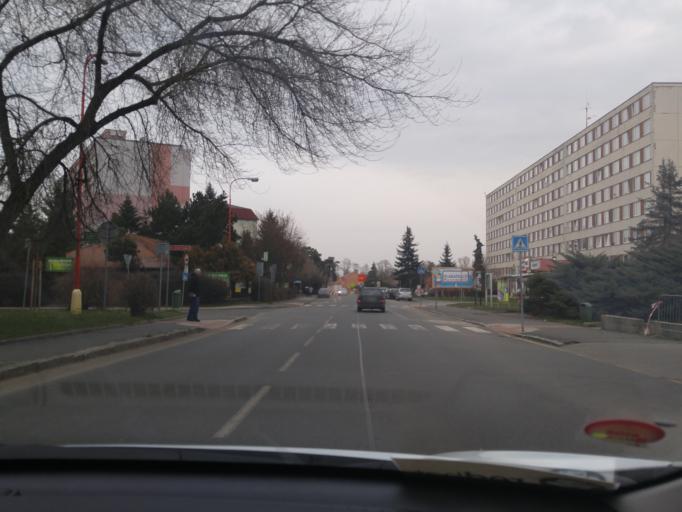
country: CZ
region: Central Bohemia
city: Neratovice
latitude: 50.2538
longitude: 14.5202
